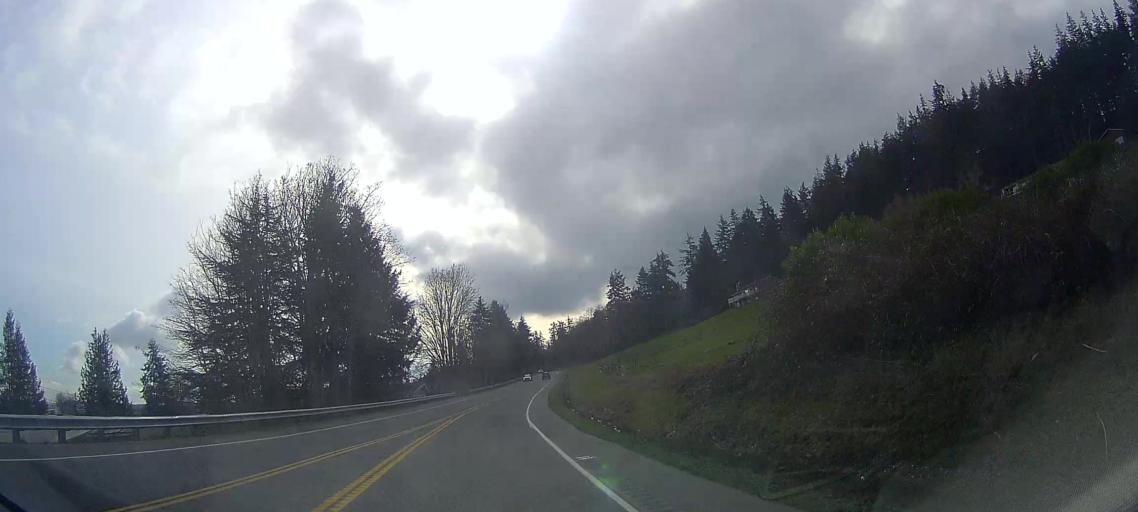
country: US
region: Washington
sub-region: Island County
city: Camano
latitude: 48.1913
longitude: -122.4795
